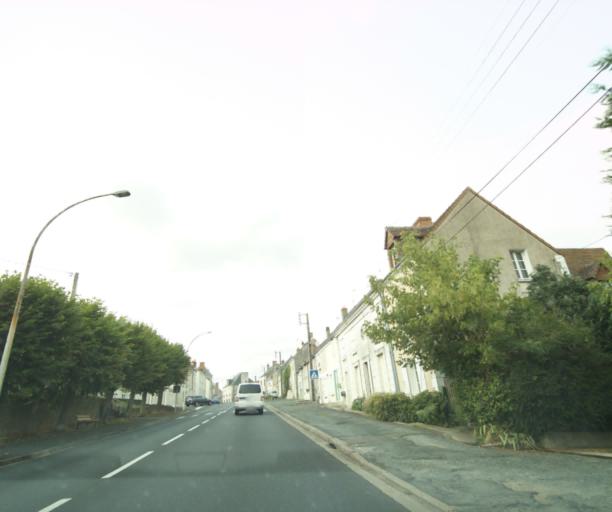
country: FR
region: Centre
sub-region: Departement de l'Indre
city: Chatillon-sur-Indre
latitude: 46.9817
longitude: 1.1764
